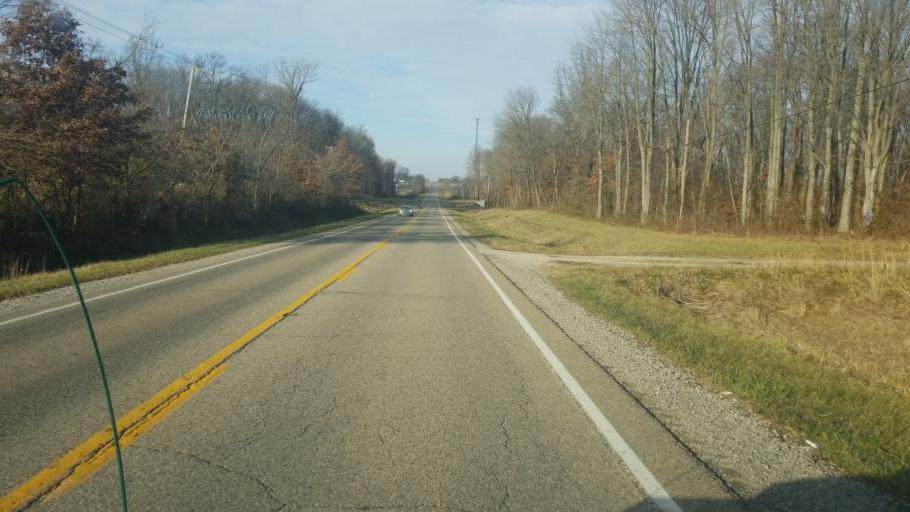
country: US
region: Illinois
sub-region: Lawrence County
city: Lawrenceville
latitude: 38.6623
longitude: -87.6942
